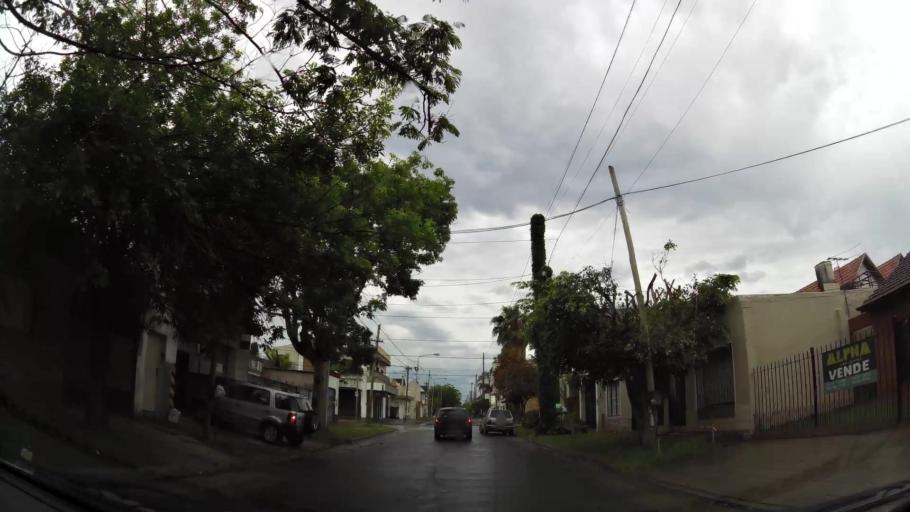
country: AR
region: Buenos Aires
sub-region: Partido de Quilmes
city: Quilmes
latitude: -34.7649
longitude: -58.2182
